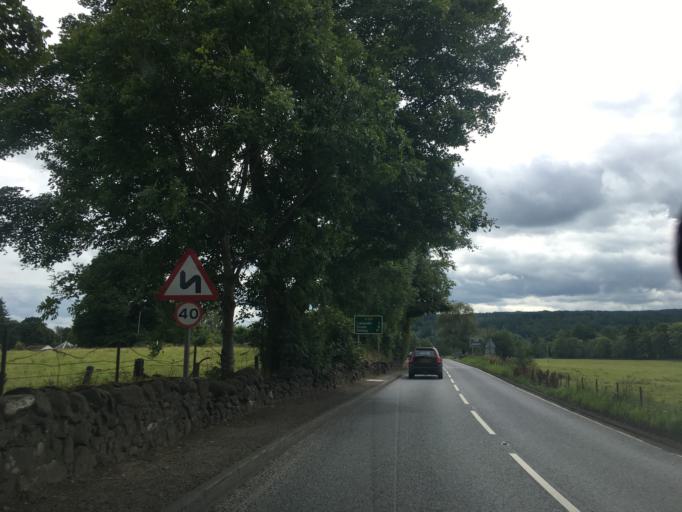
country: GB
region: Scotland
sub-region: Stirling
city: Callander
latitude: 56.2478
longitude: -4.2452
